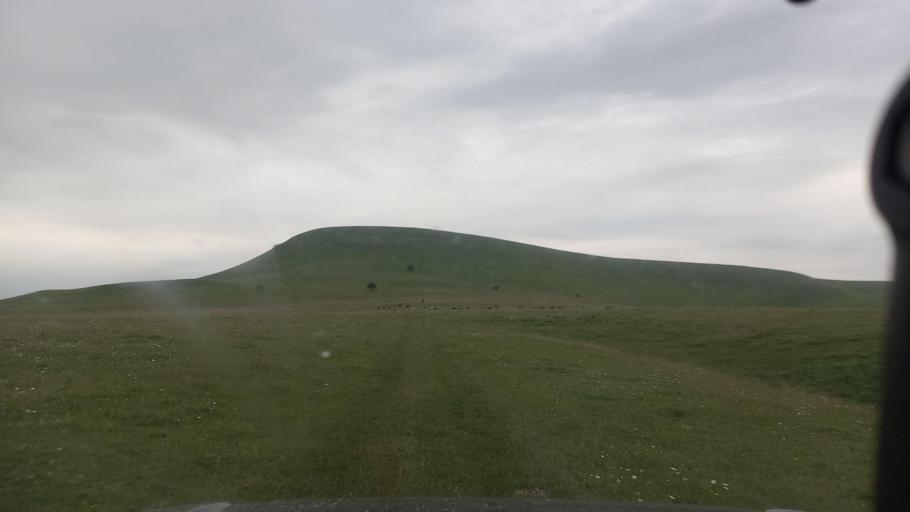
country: RU
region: Karachayevo-Cherkesiya
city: Pregradnaya
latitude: 43.9494
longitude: 41.1625
